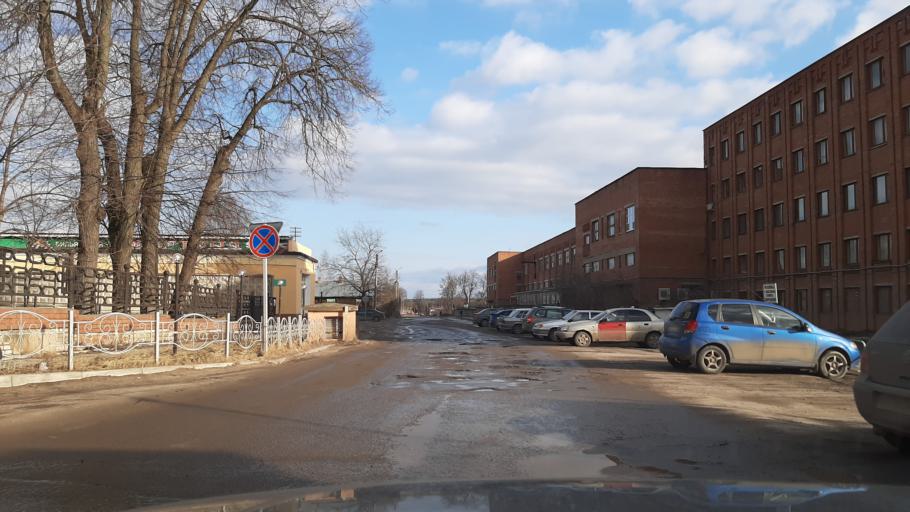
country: RU
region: Ivanovo
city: Teykovo
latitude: 56.8534
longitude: 40.5534
